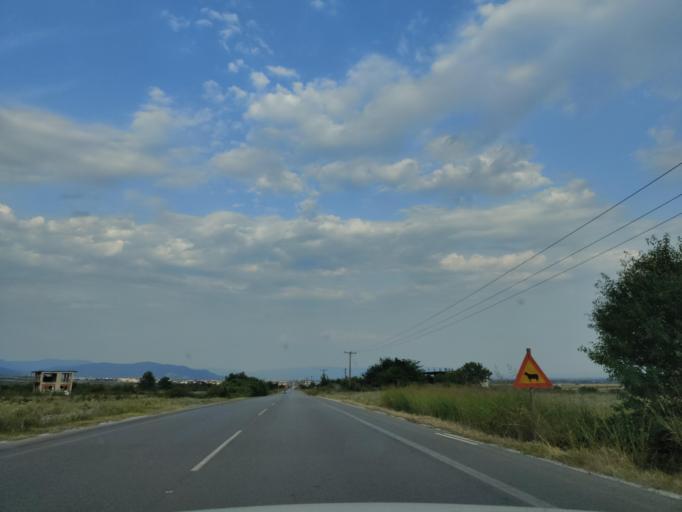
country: GR
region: East Macedonia and Thrace
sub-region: Nomos Dramas
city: Petroussa
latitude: 41.1710
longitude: 24.0340
